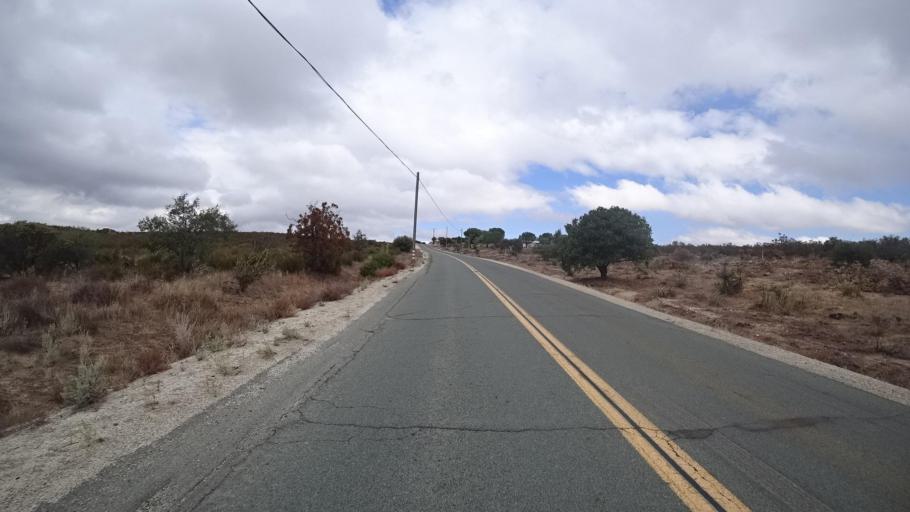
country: US
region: California
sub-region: San Diego County
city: Campo
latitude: 32.6370
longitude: -116.3203
